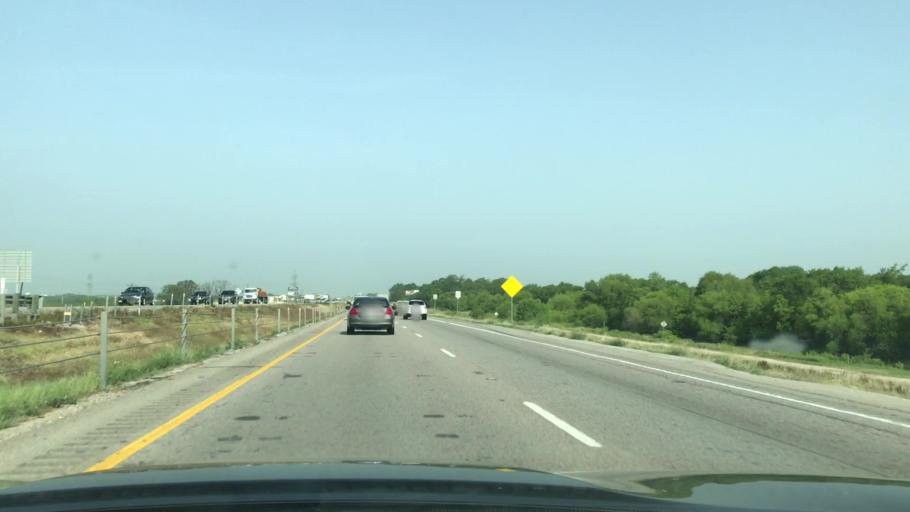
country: US
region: Texas
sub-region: Kaufman County
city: Forney
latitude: 32.7747
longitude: -96.5043
